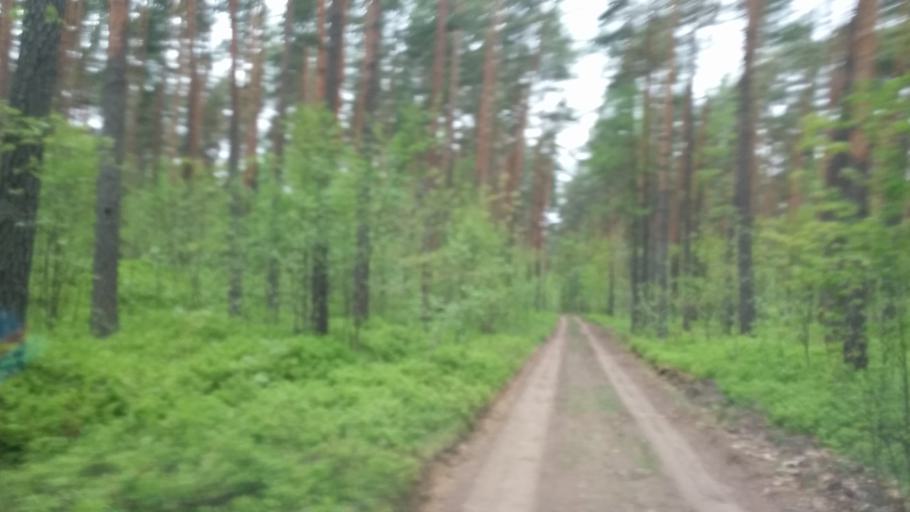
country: LV
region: Babite
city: Pinki
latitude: 56.9404
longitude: 23.9291
